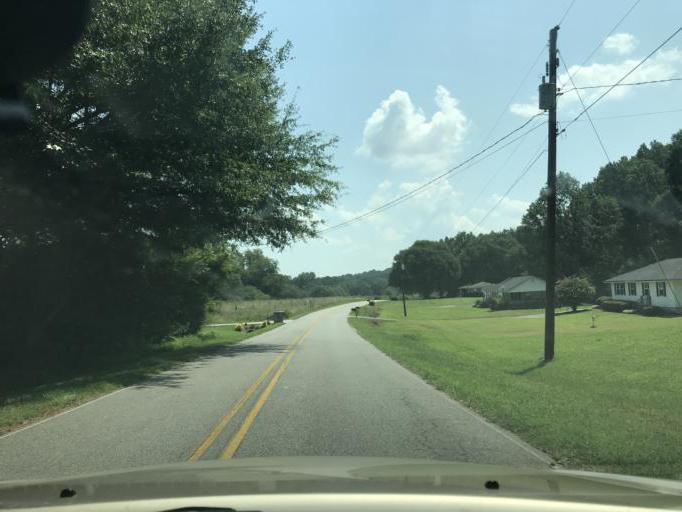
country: US
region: Georgia
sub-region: Forsyth County
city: Cumming
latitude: 34.3104
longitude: -84.1109
